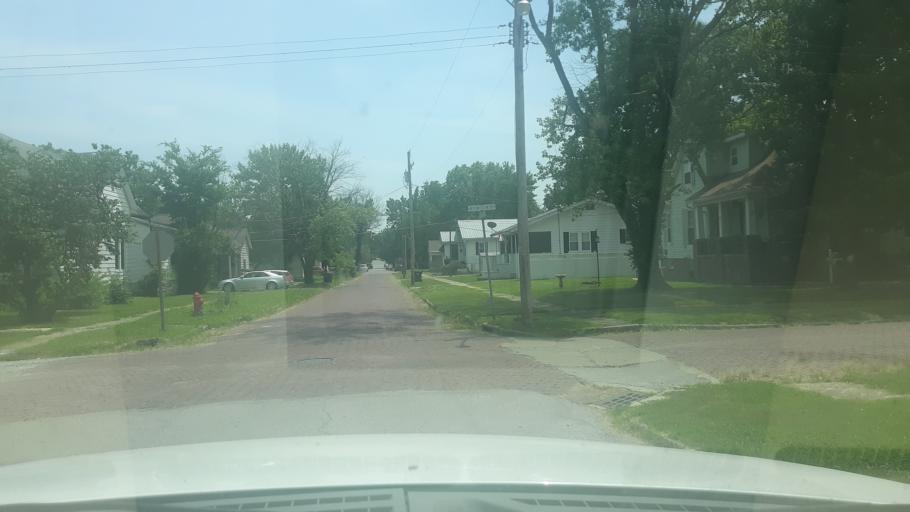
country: US
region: Illinois
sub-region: Saline County
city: Harrisburg
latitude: 37.7346
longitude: -88.5436
